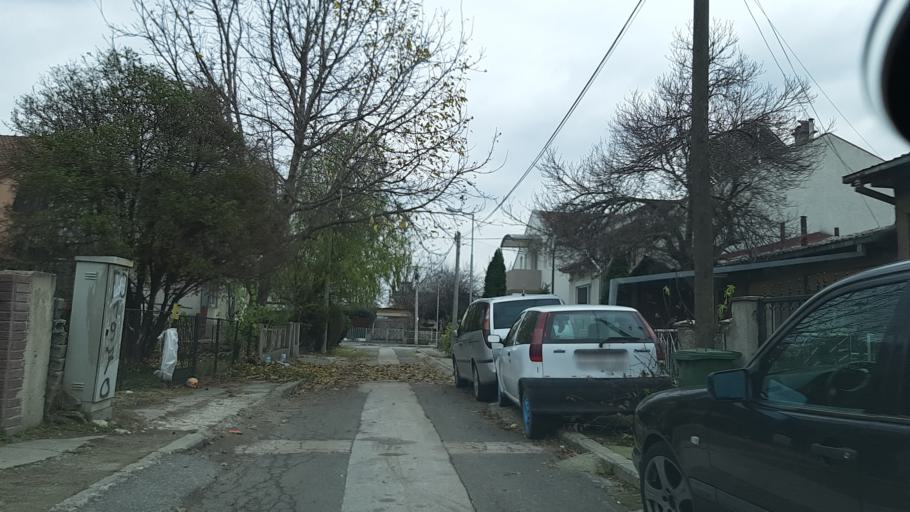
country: MK
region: Kisela Voda
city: Usje
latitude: 41.9768
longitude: 21.4676
